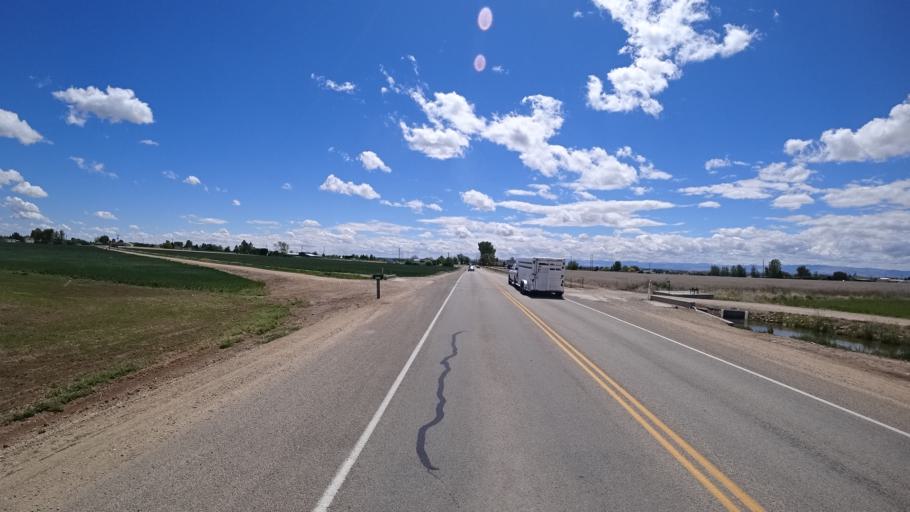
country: US
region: Idaho
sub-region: Ada County
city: Meridian
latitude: 43.5637
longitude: -116.4338
